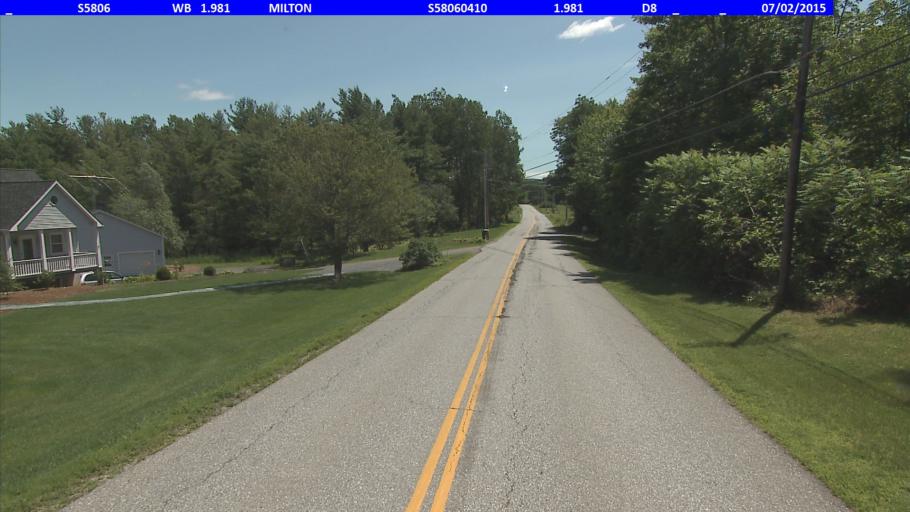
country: US
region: Vermont
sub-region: Chittenden County
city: Milton
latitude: 44.6617
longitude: -73.1492
